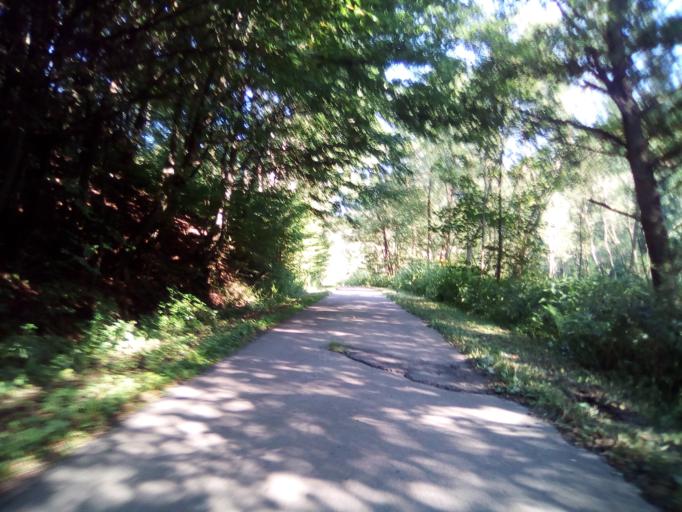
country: PL
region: Subcarpathian Voivodeship
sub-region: Powiat brzozowski
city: Domaradz
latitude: 49.8140
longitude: 21.9588
